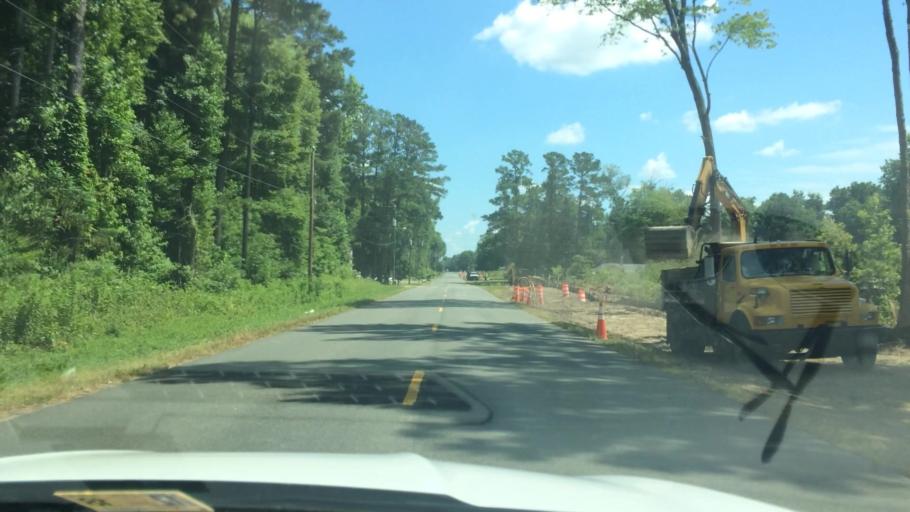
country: US
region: Virginia
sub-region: King William County
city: West Point
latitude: 37.5594
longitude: -76.8103
